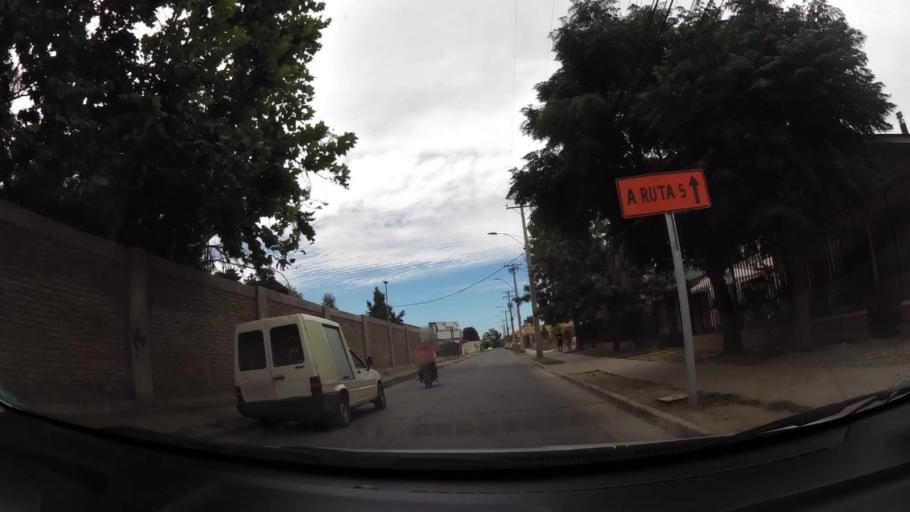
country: CL
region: O'Higgins
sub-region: Provincia de Cachapoal
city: Graneros
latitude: -34.0708
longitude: -70.7211
